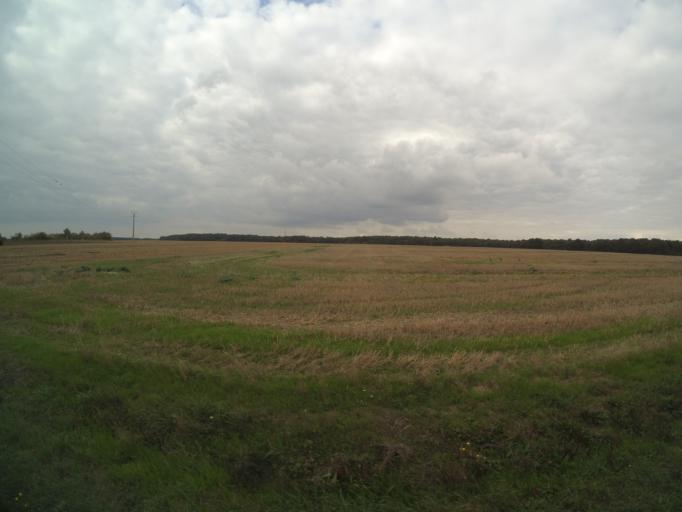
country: FR
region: Centre
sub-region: Departement d'Indre-et-Loire
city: Poce-sur-Cisse
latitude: 47.5025
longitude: 0.9768
